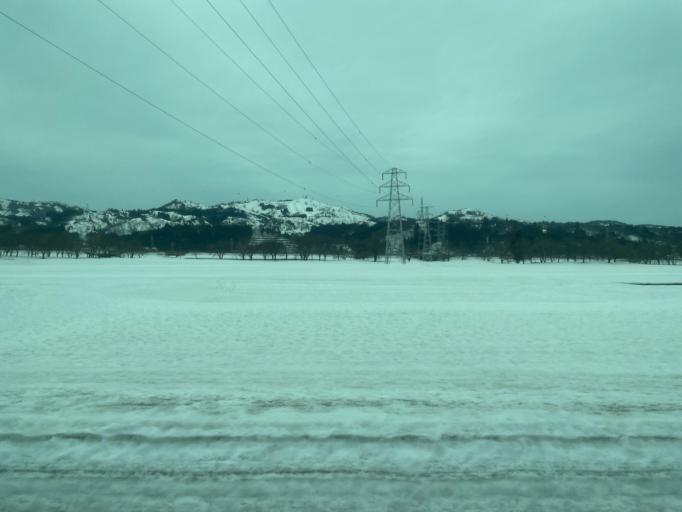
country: JP
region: Niigata
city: Shiozawa
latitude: 37.0518
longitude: 138.8647
